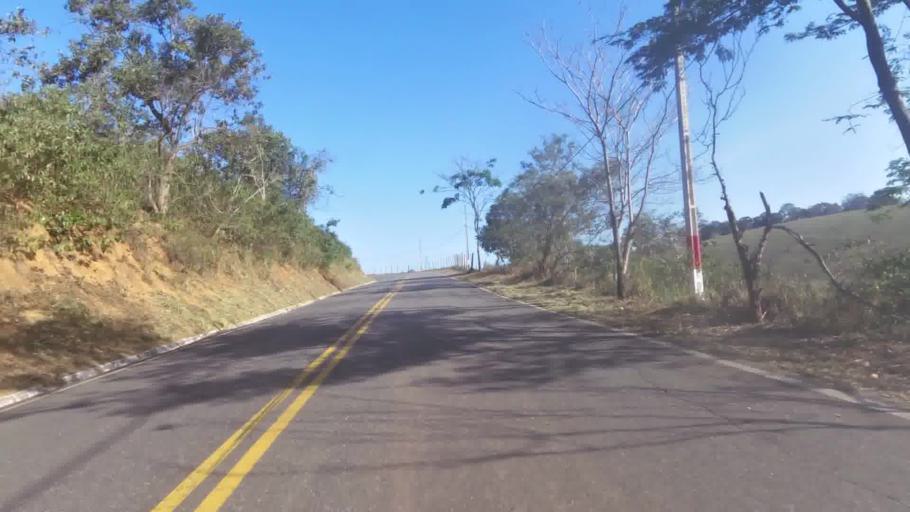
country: BR
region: Espirito Santo
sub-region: Iconha
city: Iconha
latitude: -20.7356
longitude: -40.7670
